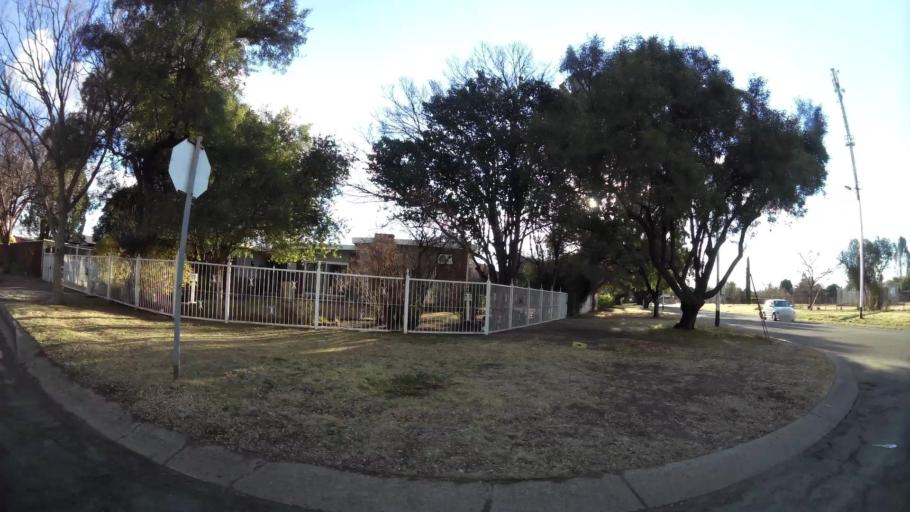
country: ZA
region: North-West
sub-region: Dr Kenneth Kaunda District Municipality
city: Potchefstroom
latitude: -26.7417
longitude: 27.0893
